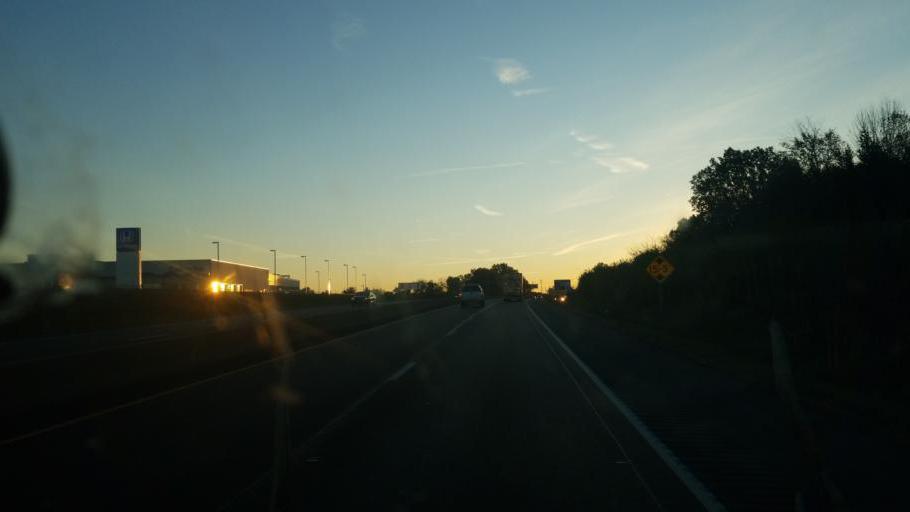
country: US
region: Missouri
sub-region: Boone County
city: Columbia
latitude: 38.9682
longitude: -92.3154
